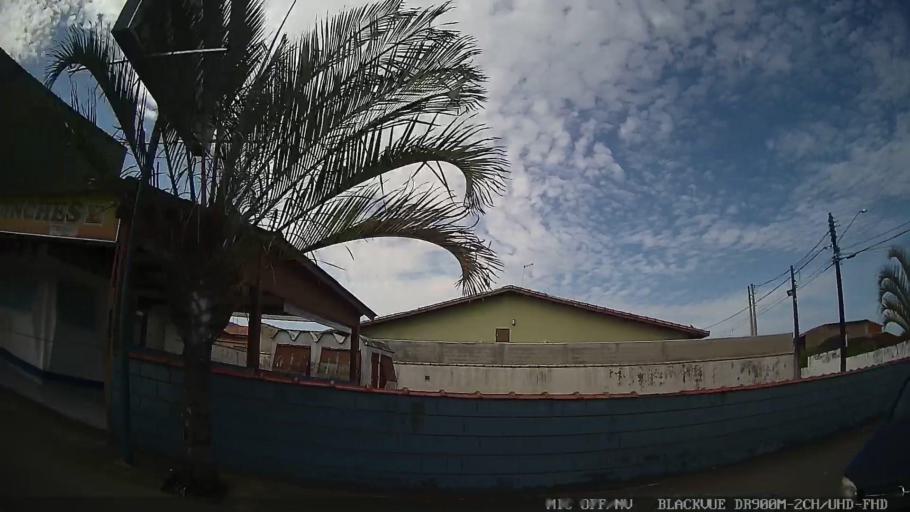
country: BR
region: Sao Paulo
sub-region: Itanhaem
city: Itanhaem
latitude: -24.1594
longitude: -46.7662
